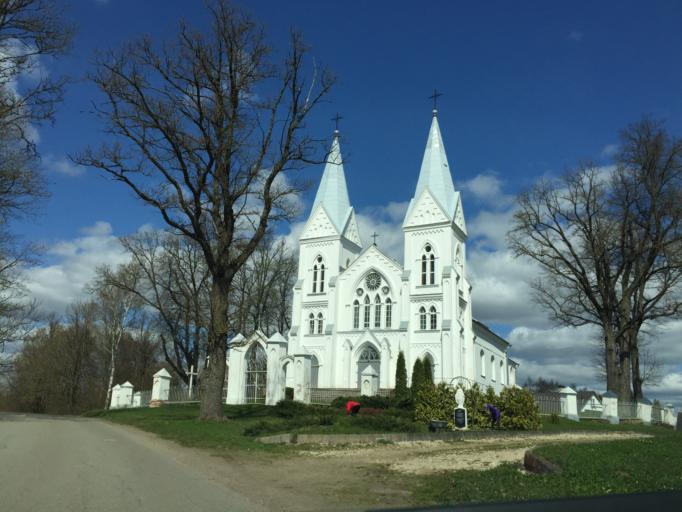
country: LV
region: Vilanu
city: Vilani
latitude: 56.7370
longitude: 27.0674
